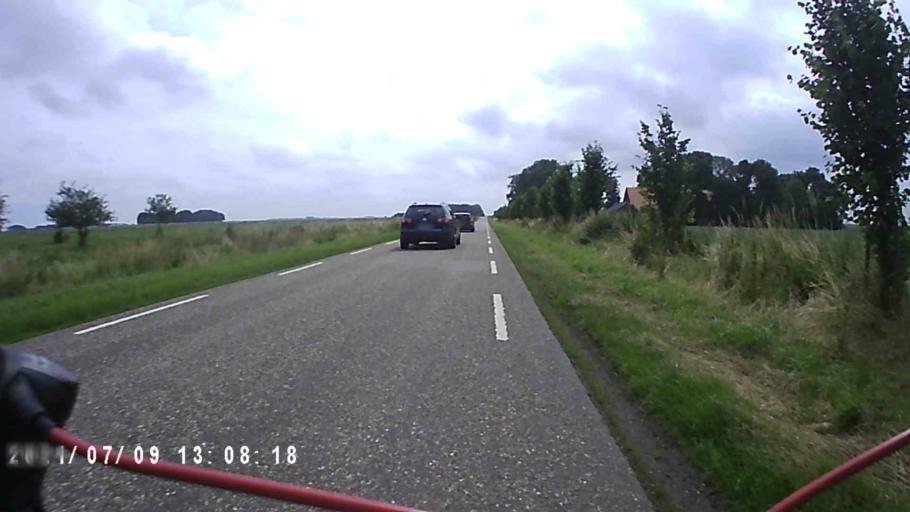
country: NL
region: Groningen
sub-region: Gemeente  Oldambt
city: Winschoten
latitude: 53.1312
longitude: 7.1104
